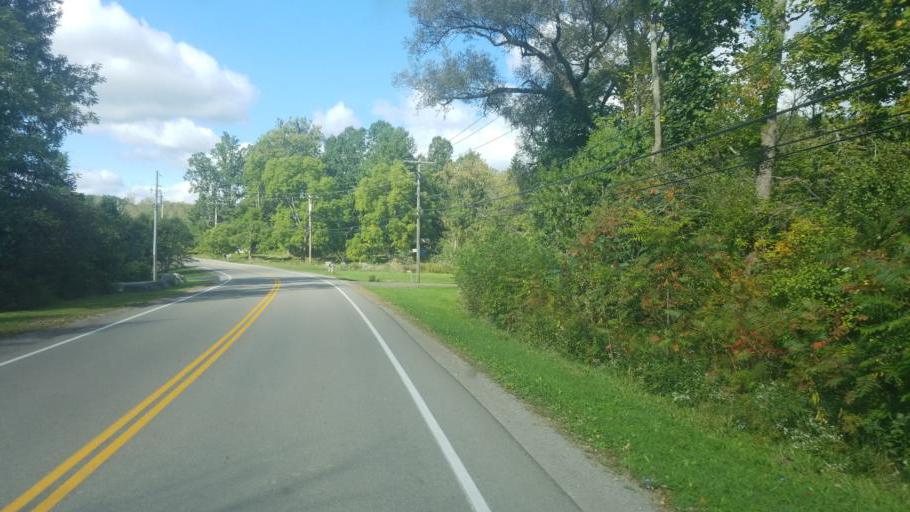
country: US
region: New York
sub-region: Allegany County
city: Cuba
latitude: 42.2541
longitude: -78.2785
